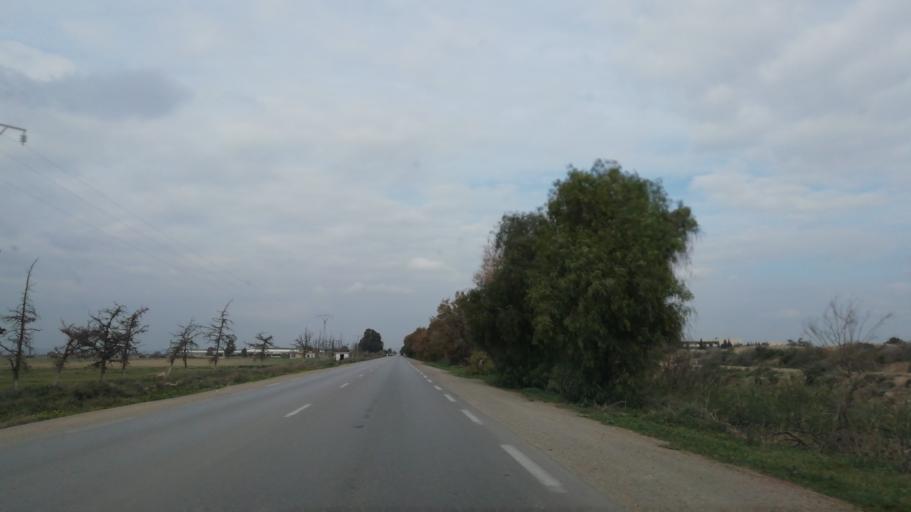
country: DZ
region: Mascara
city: Mascara
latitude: 35.6499
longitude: 0.0596
